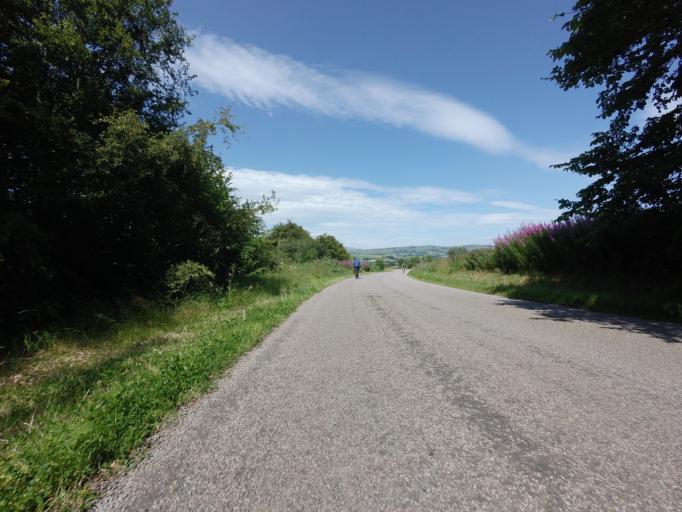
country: GB
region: Scotland
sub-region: Highland
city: Conon Bridge
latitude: 57.5652
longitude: -4.4222
